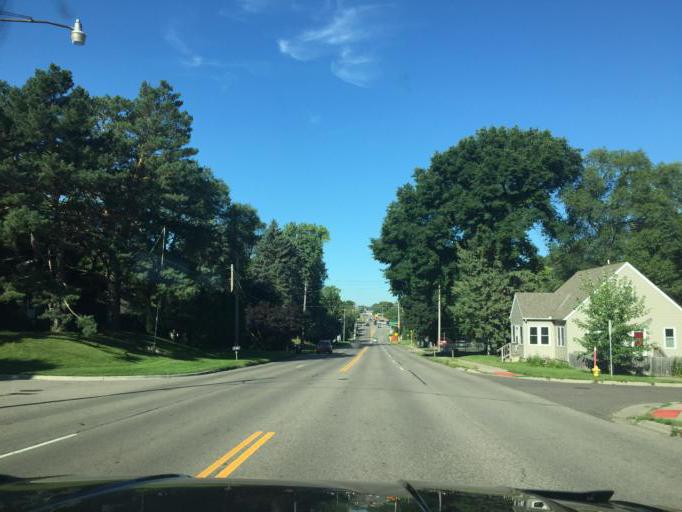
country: US
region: Minnesota
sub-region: Ramsey County
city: Little Canada
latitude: 44.9919
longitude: -93.1000
